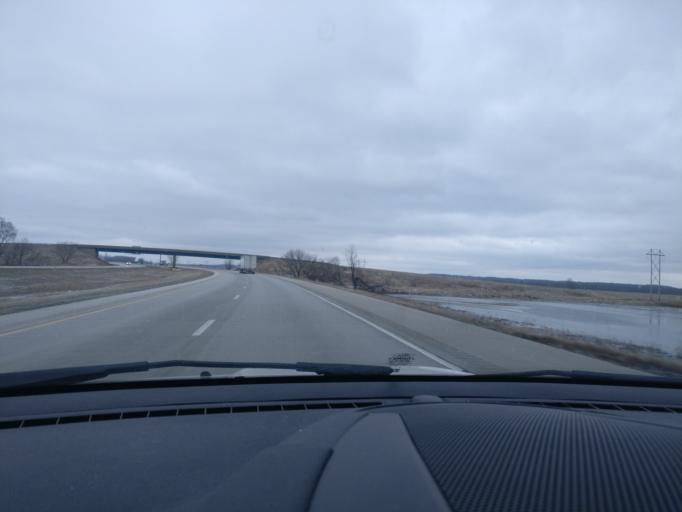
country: US
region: Illinois
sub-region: Henry County
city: Colona
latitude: 41.5337
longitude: -90.3134
